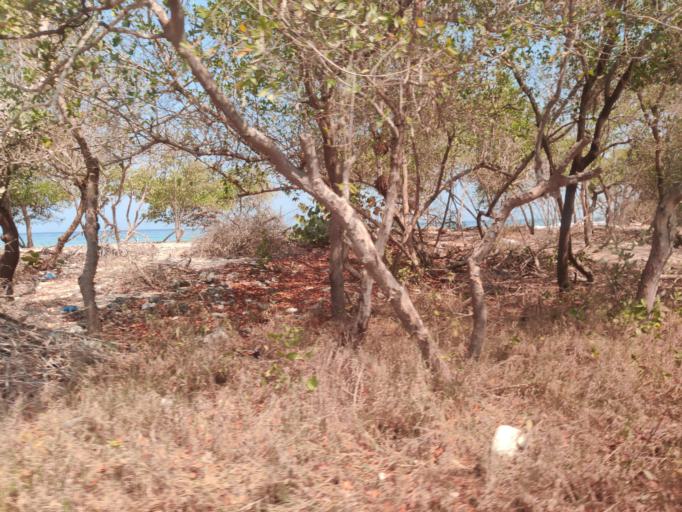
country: CO
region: Bolivar
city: Turbana
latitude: 10.1858
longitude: -75.6410
